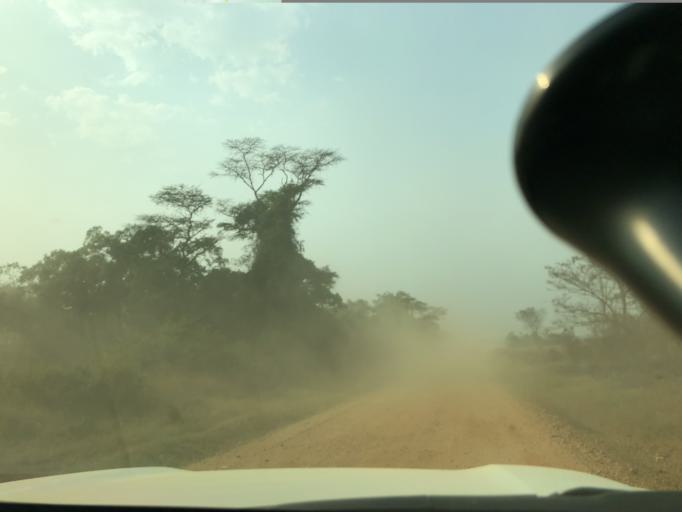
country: CD
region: Nord Kivu
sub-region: North Kivu
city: Butembo
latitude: 0.0868
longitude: 29.6438
